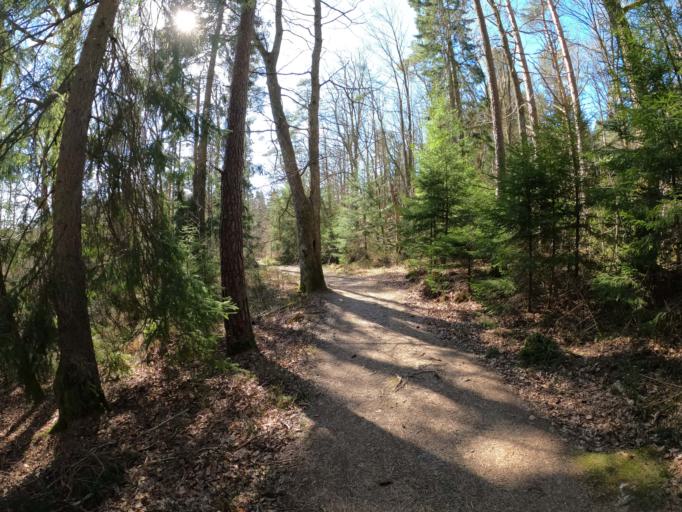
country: SE
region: Vaestra Goetaland
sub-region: Harryda Kommun
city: Molnlycke
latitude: 57.6401
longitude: 12.1290
